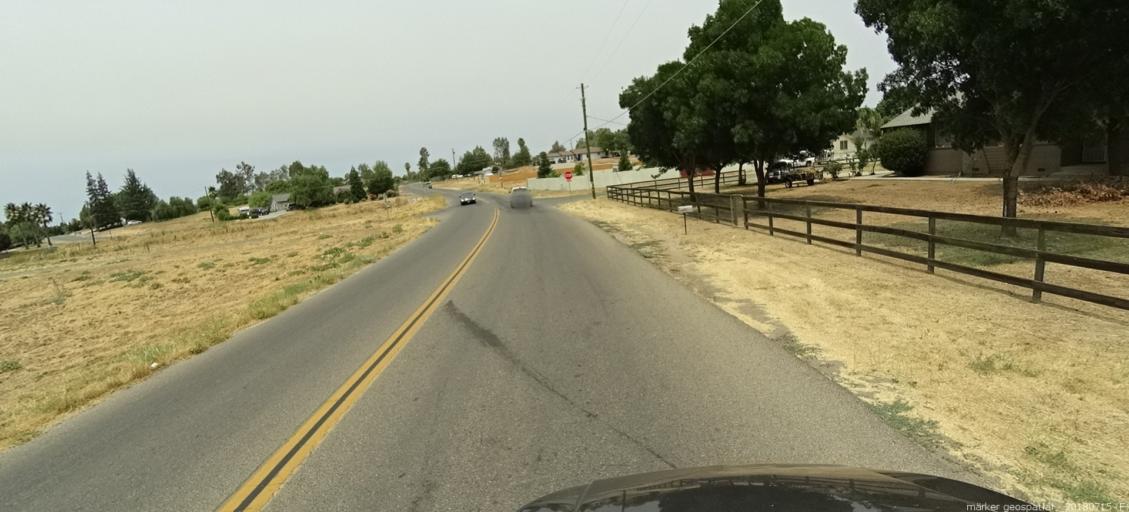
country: US
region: California
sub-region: Madera County
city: Madera Acres
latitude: 37.0007
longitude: -120.0883
